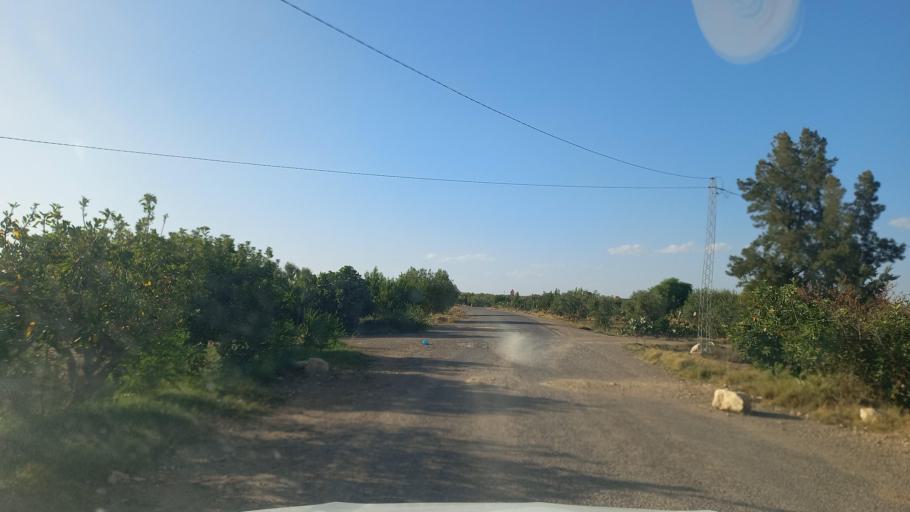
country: TN
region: Al Qasrayn
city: Kasserine
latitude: 35.2653
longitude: 9.0280
